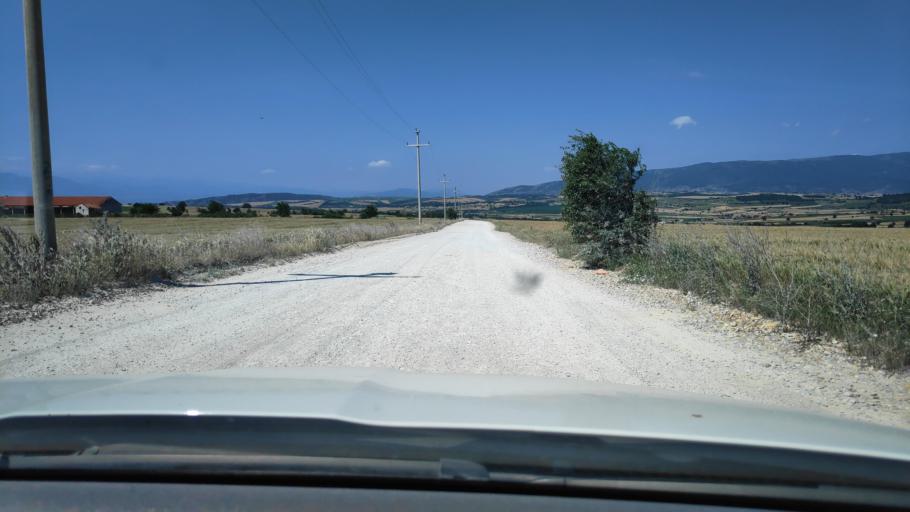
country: MK
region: Kumanovo
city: Romanovce
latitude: 42.0788
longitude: 21.7253
